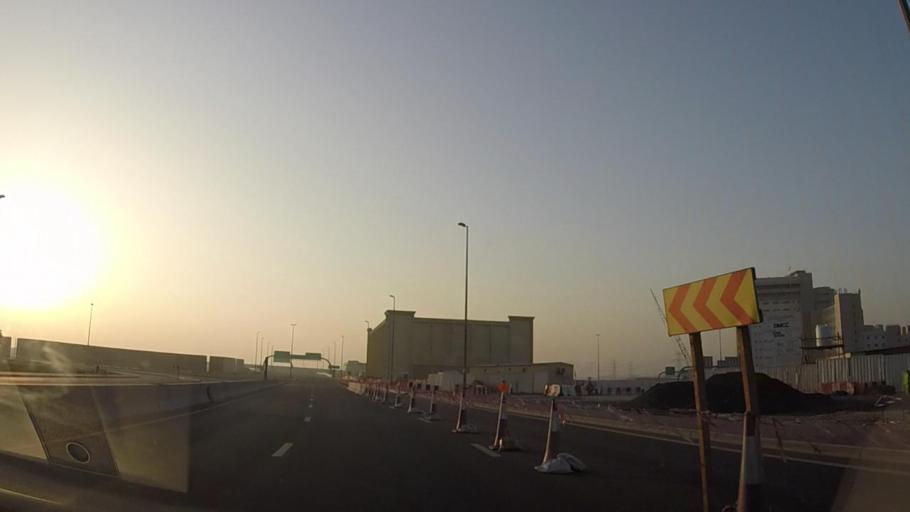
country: AE
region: Dubai
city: Dubai
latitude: 25.0620
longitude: 55.1372
